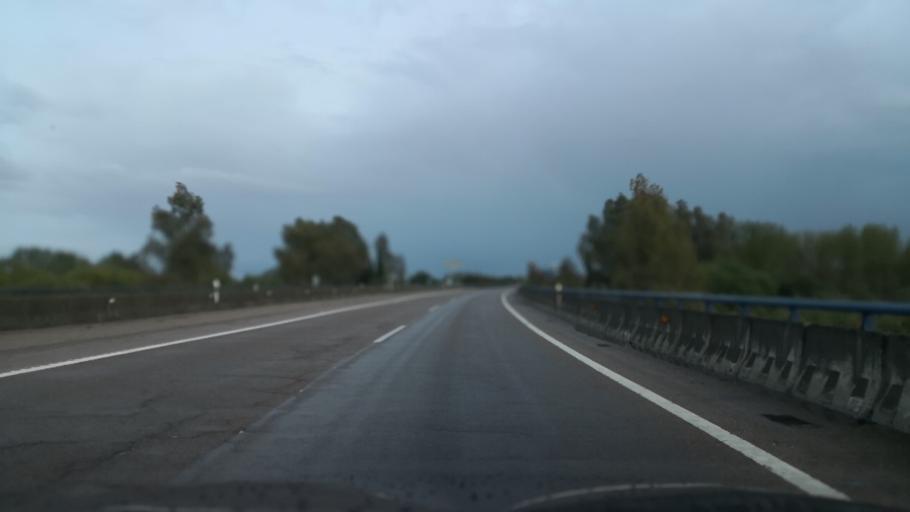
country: ES
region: Extremadura
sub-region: Provincia de Badajoz
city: Badajoz
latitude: 38.9197
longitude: -6.9575
